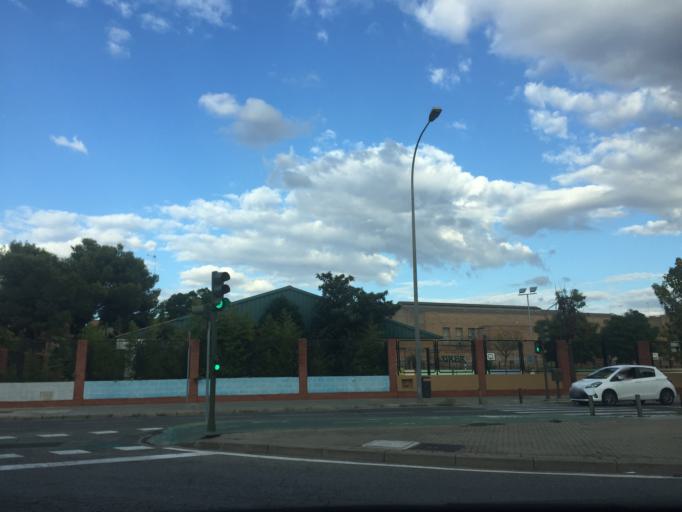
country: ES
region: Andalusia
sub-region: Provincia de Sevilla
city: Sevilla
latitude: 37.3651
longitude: -5.9640
